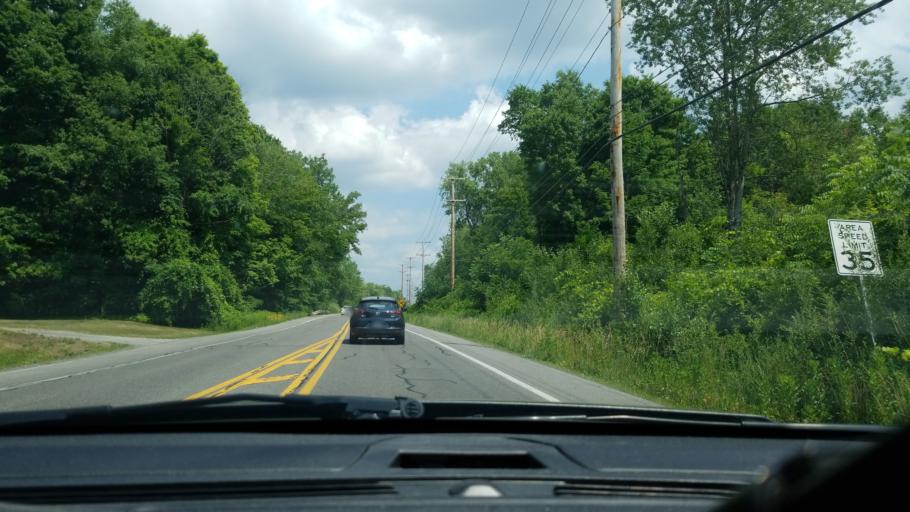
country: US
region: New York
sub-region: Onondaga County
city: Liverpool
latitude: 43.1505
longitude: -76.2062
